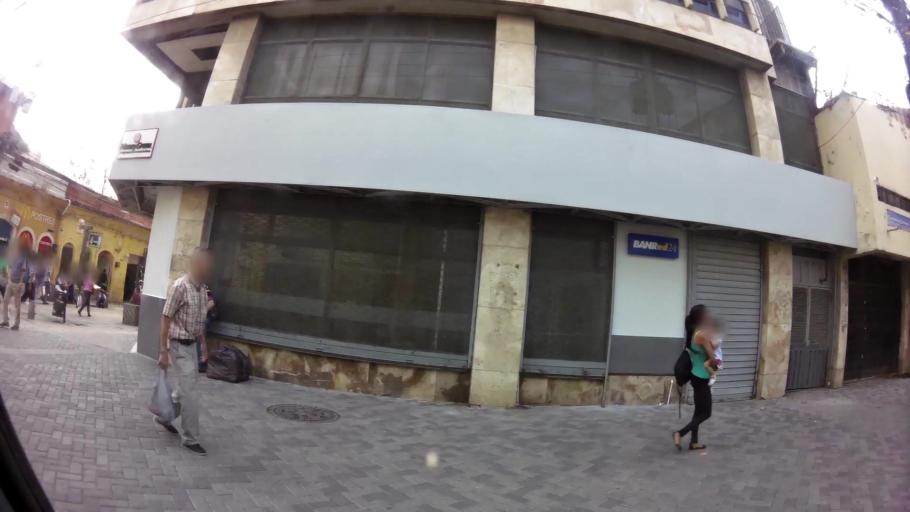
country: HN
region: Francisco Morazan
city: Tegucigalpa
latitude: 14.1063
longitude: -87.2059
